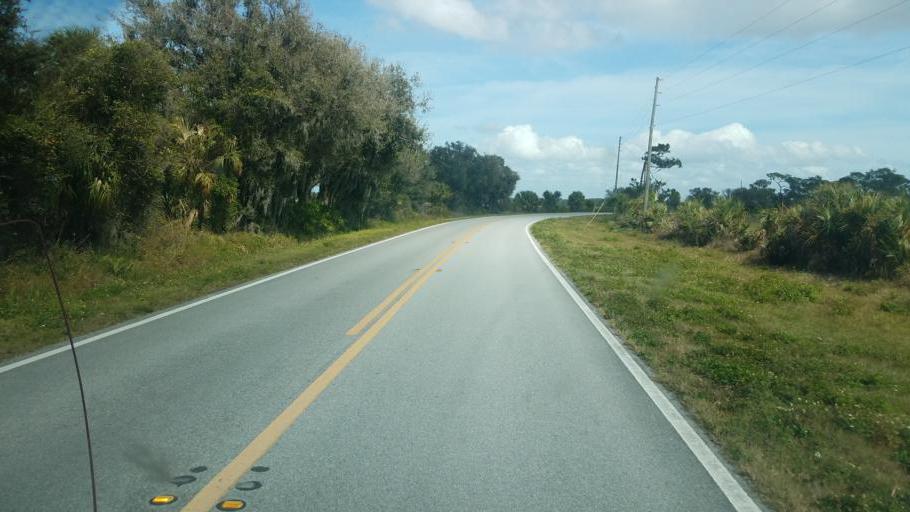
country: US
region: Florida
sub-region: Osceola County
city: Poinciana
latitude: 27.9683
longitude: -81.4012
